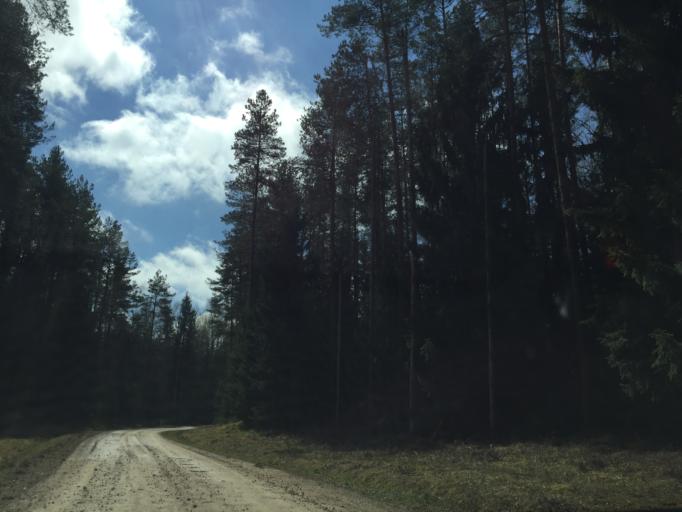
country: EE
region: Valgamaa
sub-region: Valga linn
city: Valga
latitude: 57.6107
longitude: 26.1584
